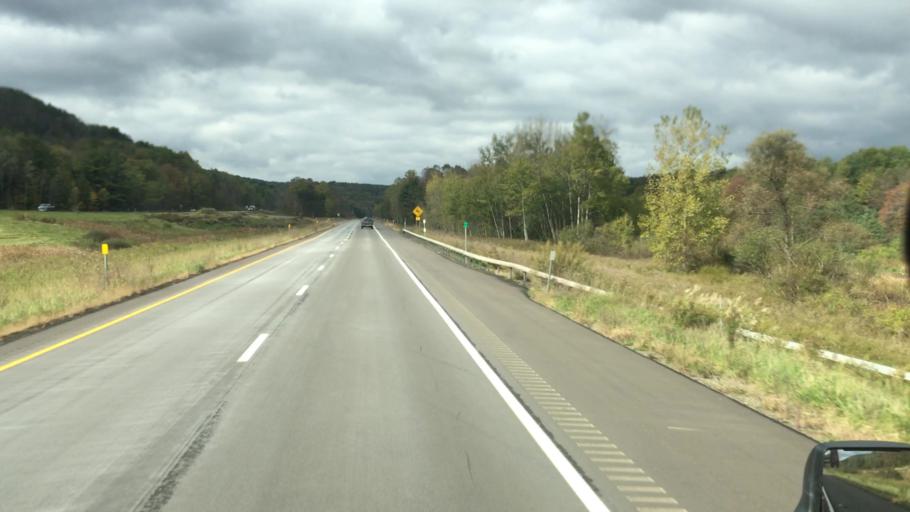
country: US
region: New York
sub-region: Cattaraugus County
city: Randolph
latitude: 42.1209
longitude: -78.9356
